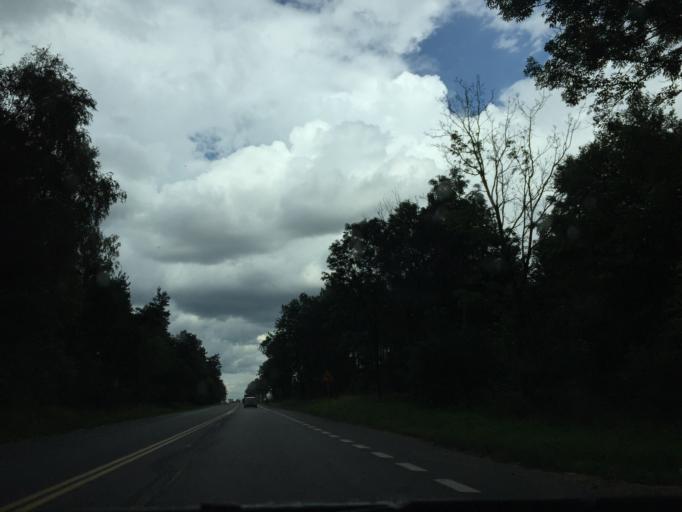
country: PL
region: Swietokrzyskie
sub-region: Powiat jedrzejowski
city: Jedrzejow
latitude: 50.6879
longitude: 20.3590
